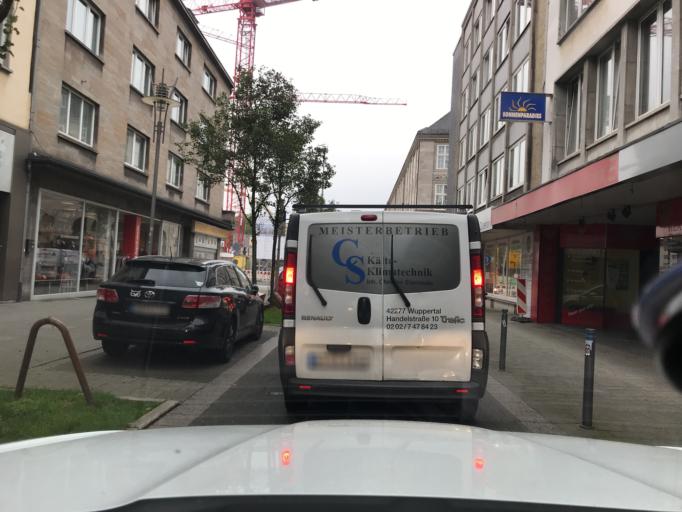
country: DE
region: North Rhine-Westphalia
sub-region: Regierungsbezirk Dusseldorf
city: Muelheim (Ruhr)
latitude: 51.4284
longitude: 6.8801
